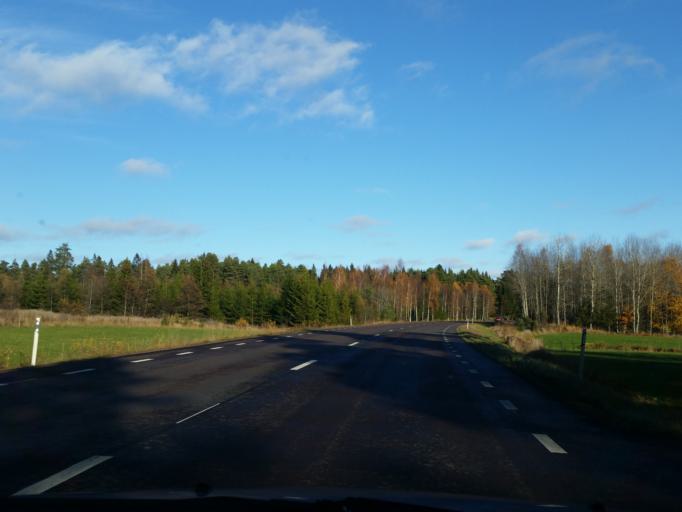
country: AX
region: Alands landsbygd
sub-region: Jomala
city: Jomala
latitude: 60.2096
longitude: 19.9593
